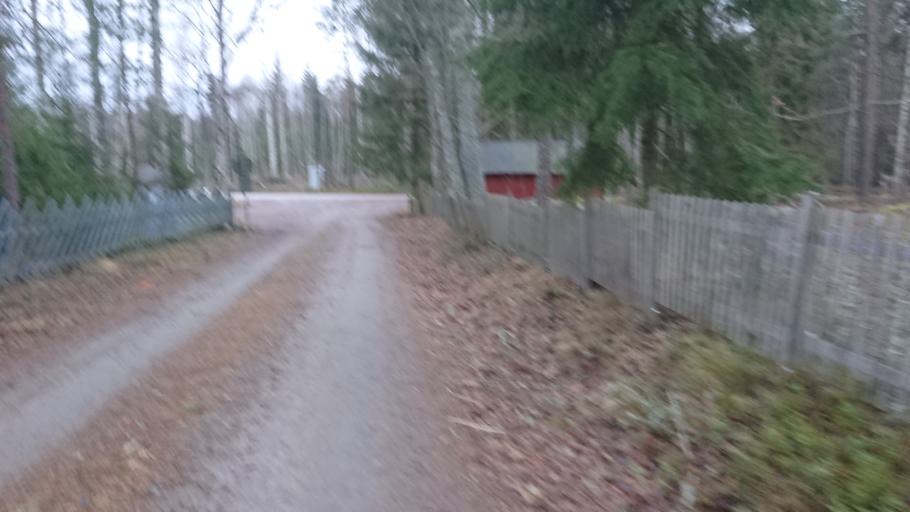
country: SE
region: Uppsala
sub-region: Osthammars Kommun
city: Bjorklinge
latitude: 60.0244
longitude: 17.5752
